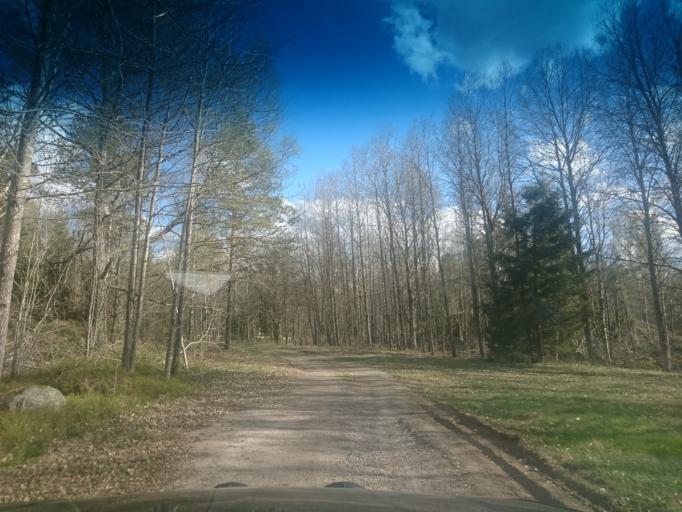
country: SE
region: Kronoberg
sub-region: Vaxjo Kommun
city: Braas
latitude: 57.2288
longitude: 15.1423
